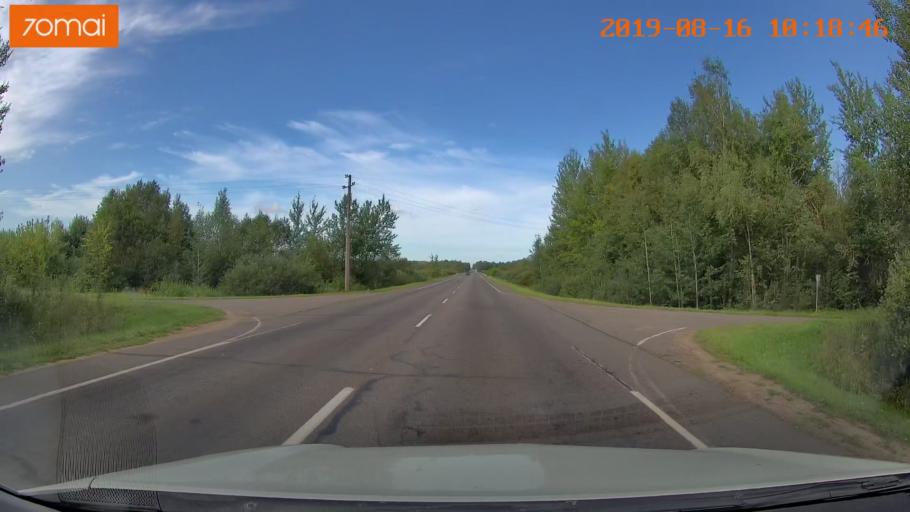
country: BY
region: Mogilev
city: Asipovichy
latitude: 53.3060
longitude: 28.6824
